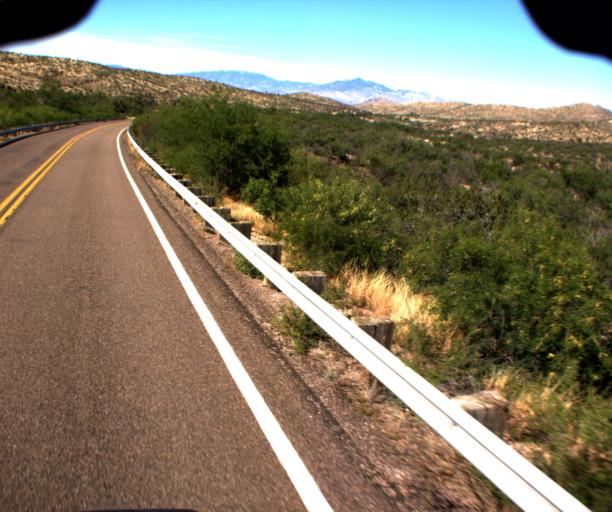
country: US
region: Arizona
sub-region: Pima County
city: Corona de Tucson
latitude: 31.8810
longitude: -110.6746
